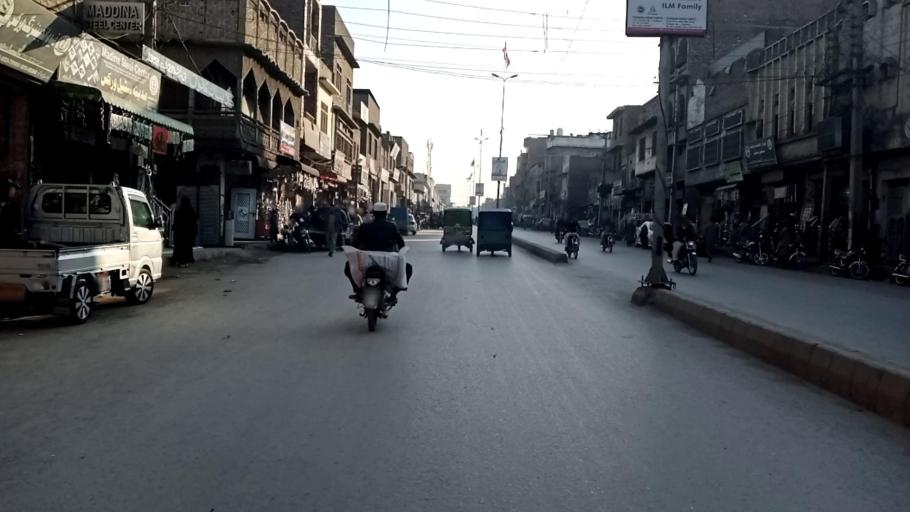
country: PK
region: Khyber Pakhtunkhwa
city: Peshawar
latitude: 34.0087
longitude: 71.5850
